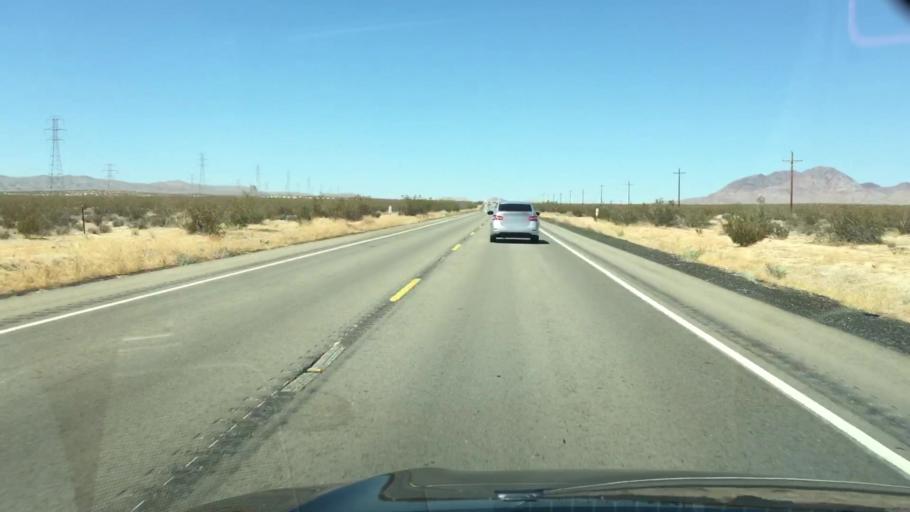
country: US
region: California
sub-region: Kern County
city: Boron
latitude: 35.2449
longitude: -117.6106
